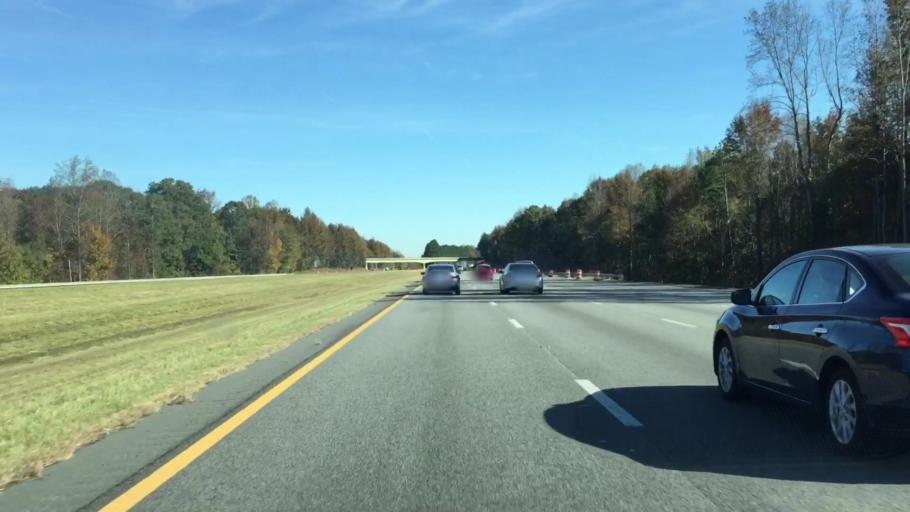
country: US
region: North Carolina
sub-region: Davidson County
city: Lexington
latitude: 35.8137
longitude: -80.1783
